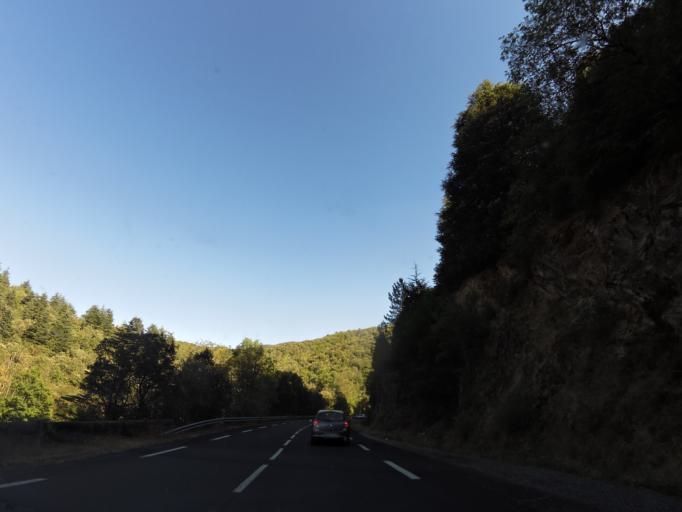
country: FR
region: Languedoc-Roussillon
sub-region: Departement du Gard
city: Valleraugue
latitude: 44.0471
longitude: 3.6855
